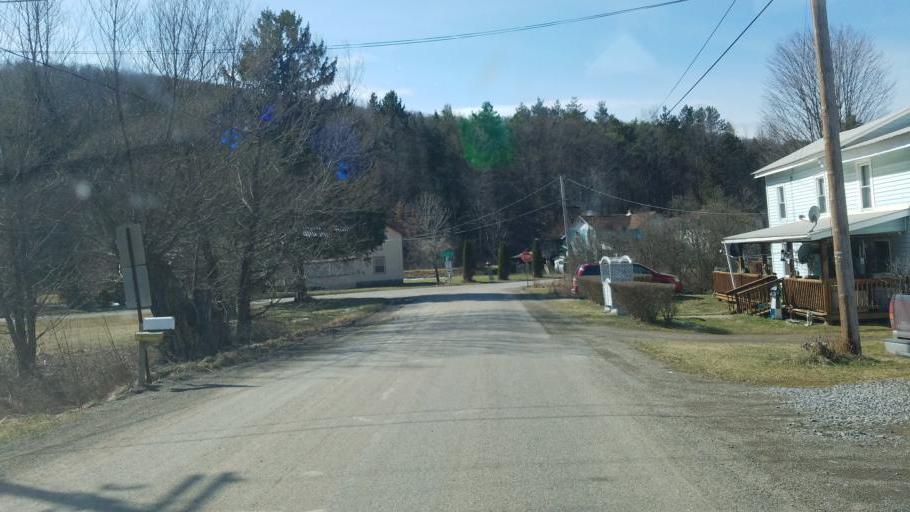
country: US
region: New York
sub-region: Allegany County
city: Andover
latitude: 41.9447
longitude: -77.8167
